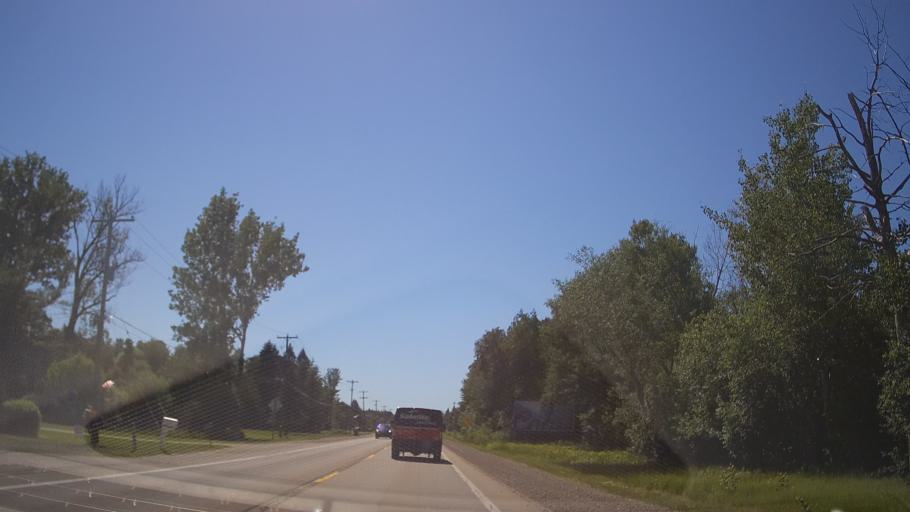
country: US
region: Michigan
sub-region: Emmet County
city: Petoskey
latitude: 45.4243
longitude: -84.8517
